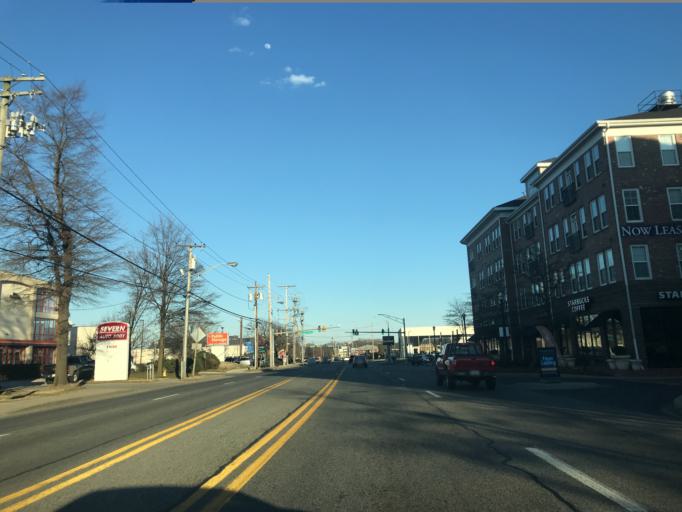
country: US
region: Maryland
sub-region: Anne Arundel County
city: Parole
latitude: 38.9799
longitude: -76.5248
